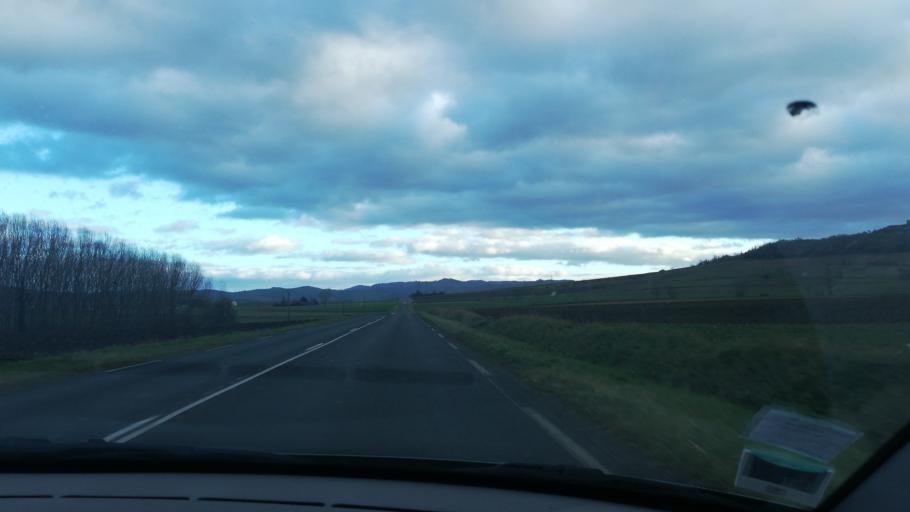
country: FR
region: Auvergne
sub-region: Departement du Puy-de-Dome
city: Vertaizon
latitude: 45.7562
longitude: 3.3144
